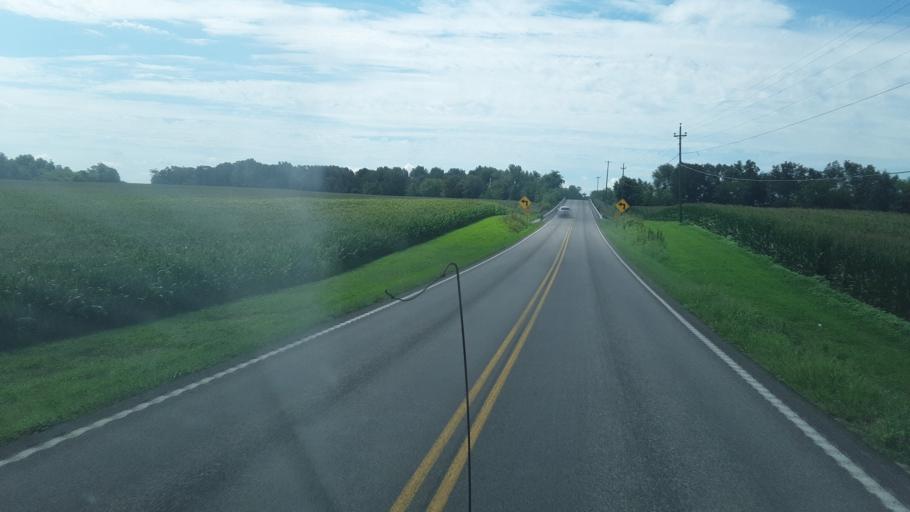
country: US
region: Kentucky
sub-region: Christian County
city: Oak Grove
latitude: 36.7592
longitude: -87.3209
